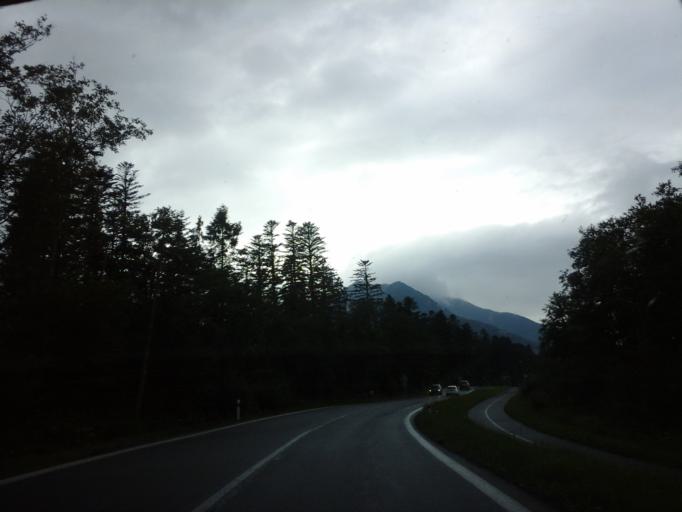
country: SK
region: Presovsky
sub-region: Okres Poprad
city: Zdiar
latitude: 49.2133
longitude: 20.3471
